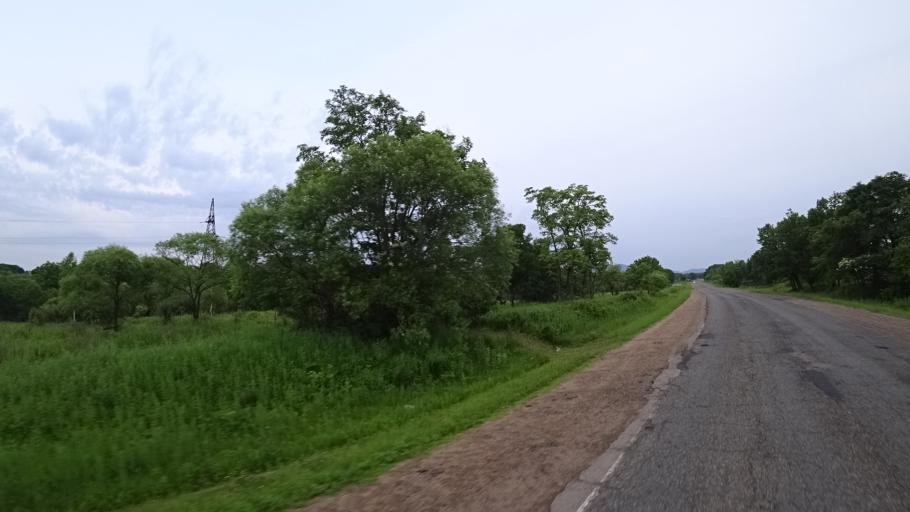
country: RU
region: Primorskiy
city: Novosysoyevka
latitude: 44.2230
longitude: 133.3502
